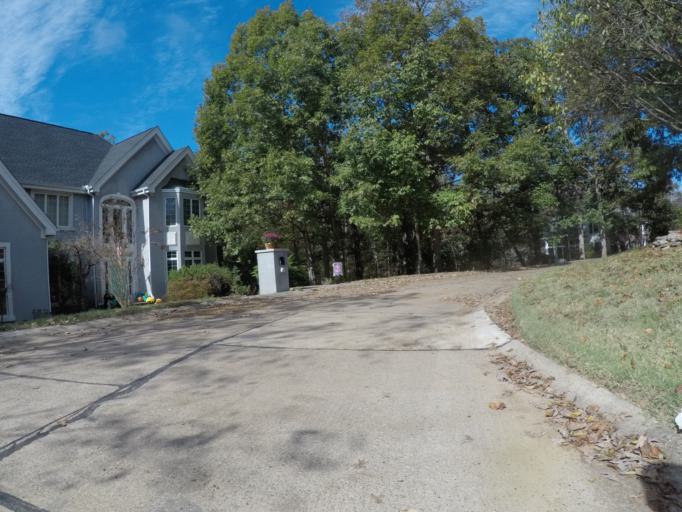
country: US
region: West Virginia
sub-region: Cabell County
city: Huntington
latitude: 38.3911
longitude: -82.3917
